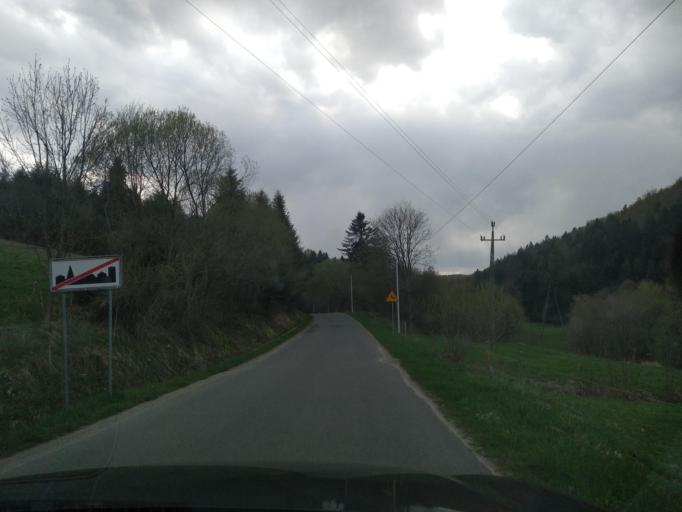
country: PL
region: Subcarpathian Voivodeship
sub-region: Powiat leski
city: Baligrod
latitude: 49.3496
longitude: 22.2578
